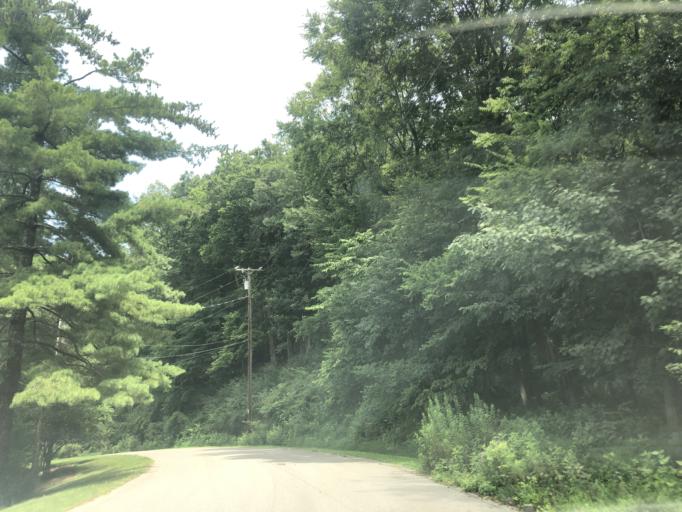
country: US
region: Tennessee
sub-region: Davidson County
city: Oak Hill
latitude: 36.0677
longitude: -86.8083
